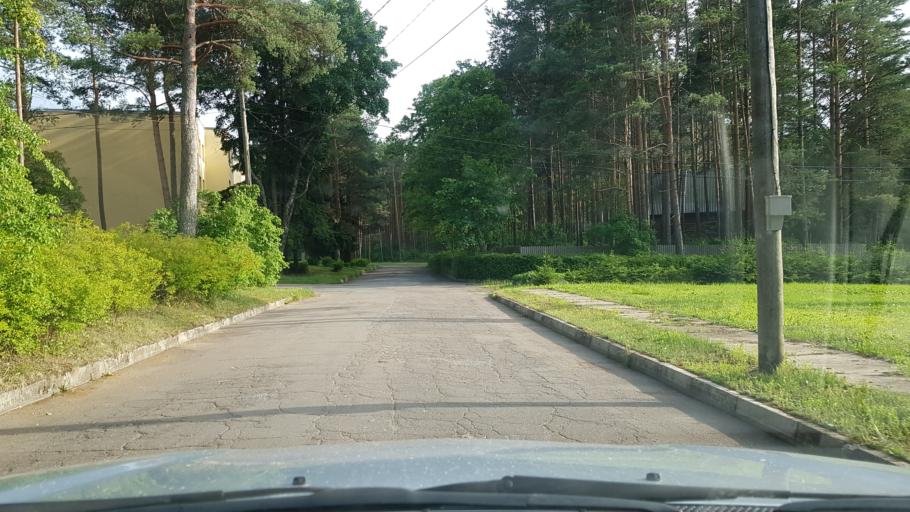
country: EE
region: Ida-Virumaa
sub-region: Narva-Joesuu linn
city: Narva-Joesuu
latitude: 59.4573
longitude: 28.0434
